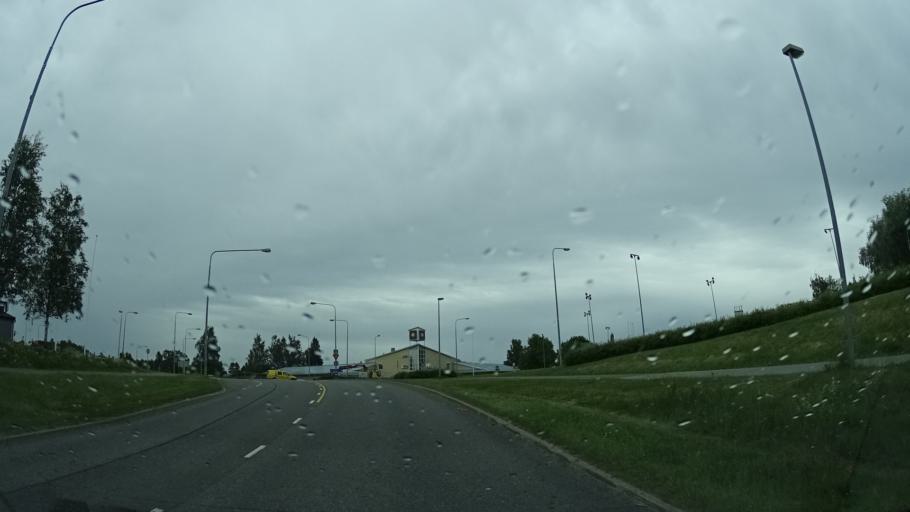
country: FI
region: Varsinais-Suomi
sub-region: Loimaa
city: Aura
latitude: 60.6474
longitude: 22.5899
